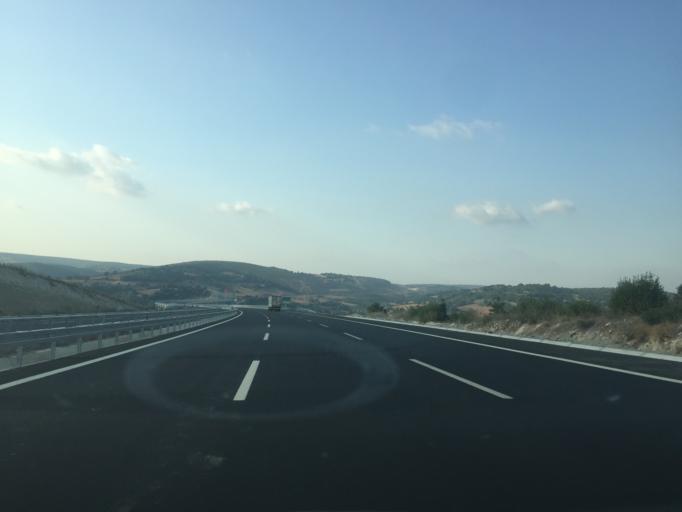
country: TR
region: Balikesir
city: Ertugrul
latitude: 39.5690
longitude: 27.7023
